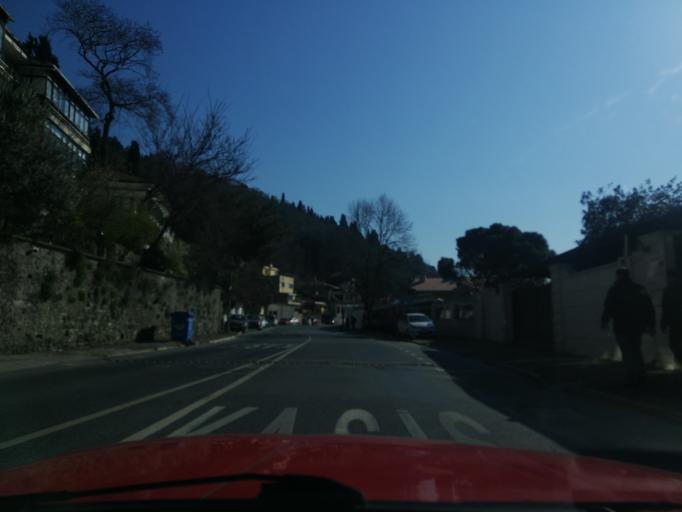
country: TR
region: Istanbul
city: UEskuedar
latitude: 41.0668
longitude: 29.0576
